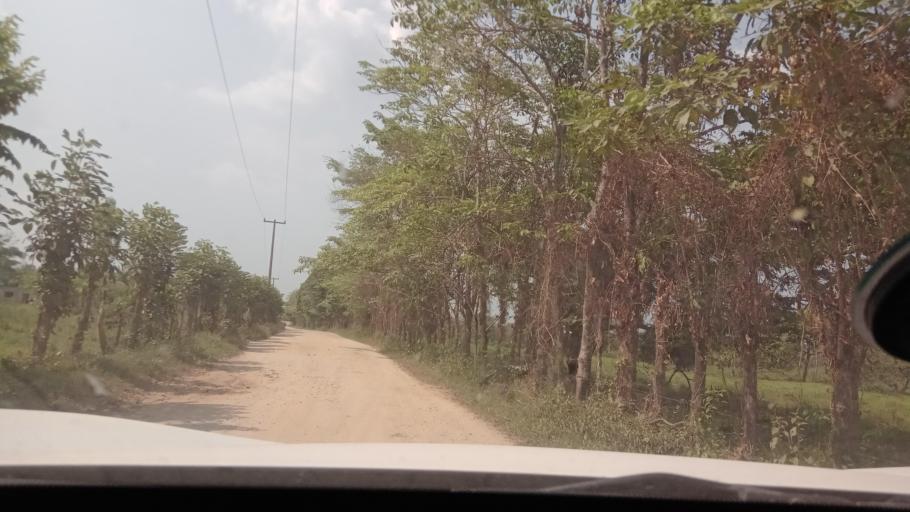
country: MX
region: Tabasco
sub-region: Huimanguillo
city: Francisco Rueda
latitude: 17.6776
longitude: -93.8620
